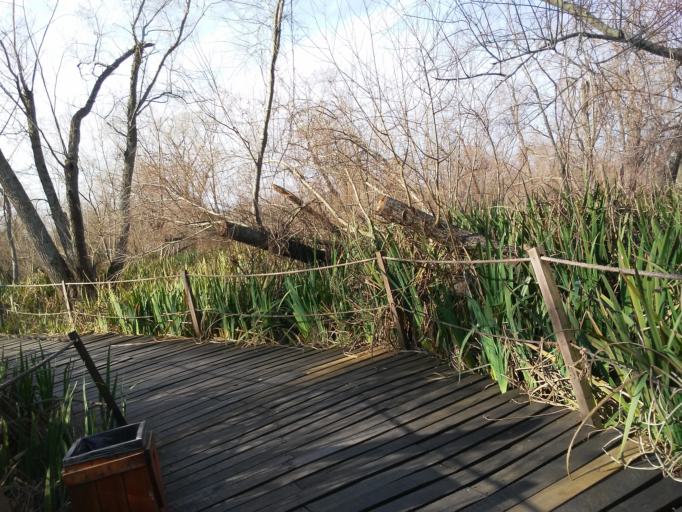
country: AR
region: Buenos Aires
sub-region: Partido de Avellaneda
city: Avellaneda
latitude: -34.6622
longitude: -58.3129
